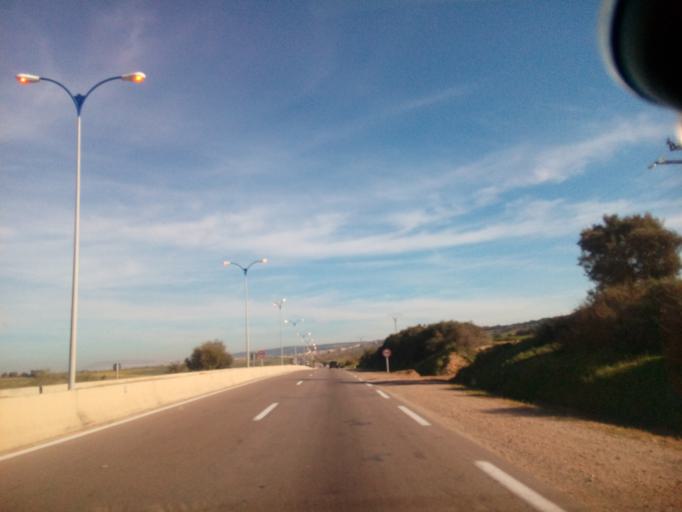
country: DZ
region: Mostaganem
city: Mostaganem
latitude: 35.8135
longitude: -0.0305
